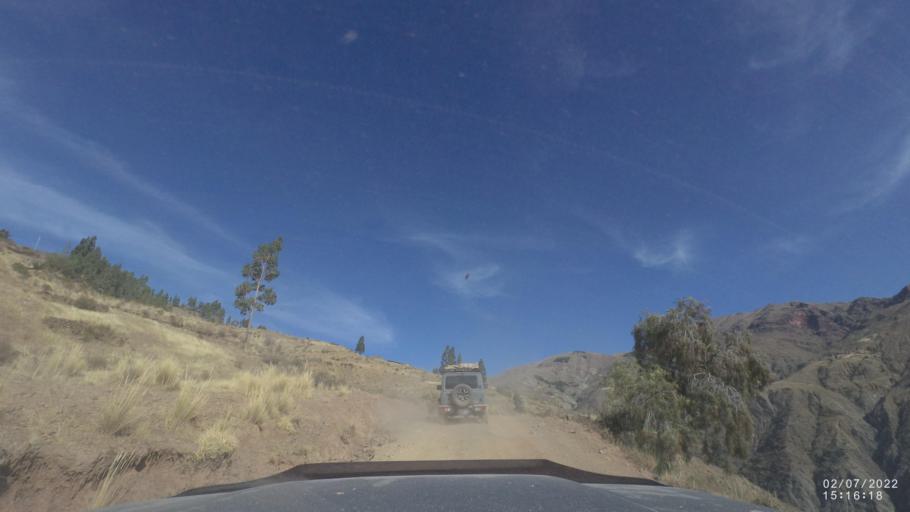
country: BO
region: Cochabamba
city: Irpa Irpa
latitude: -17.8646
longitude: -66.4333
